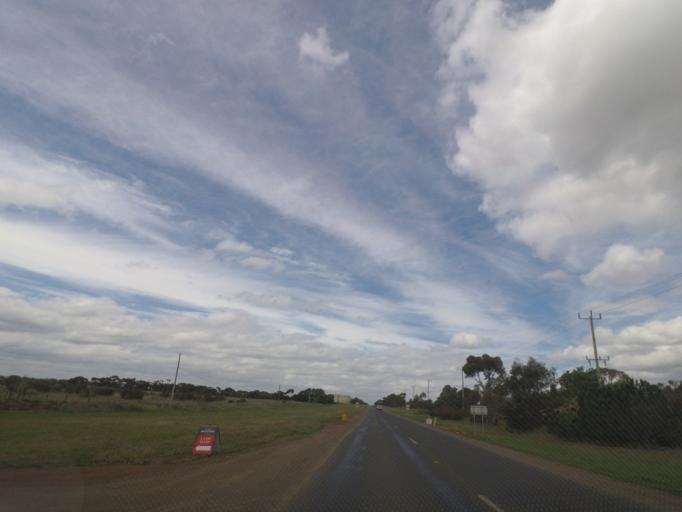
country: AU
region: Victoria
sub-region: Melton
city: Melton South
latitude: -37.7461
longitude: 144.6155
